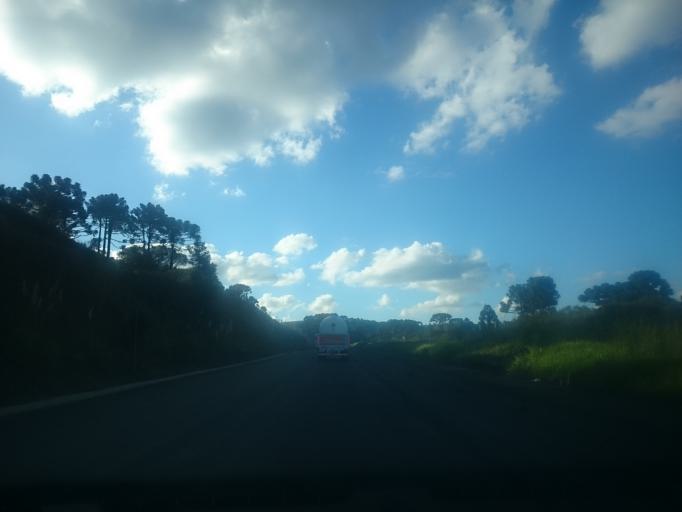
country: BR
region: Santa Catarina
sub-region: Sao Joaquim
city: Sao Joaquim
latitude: -28.0791
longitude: -50.0699
